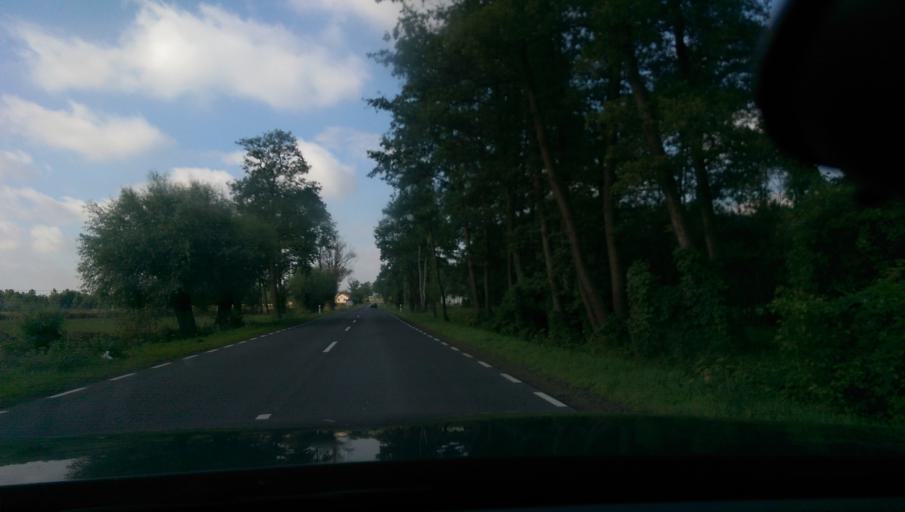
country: PL
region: Masovian Voivodeship
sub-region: Powiat plonski
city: Sochocin
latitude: 52.7096
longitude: 20.4946
